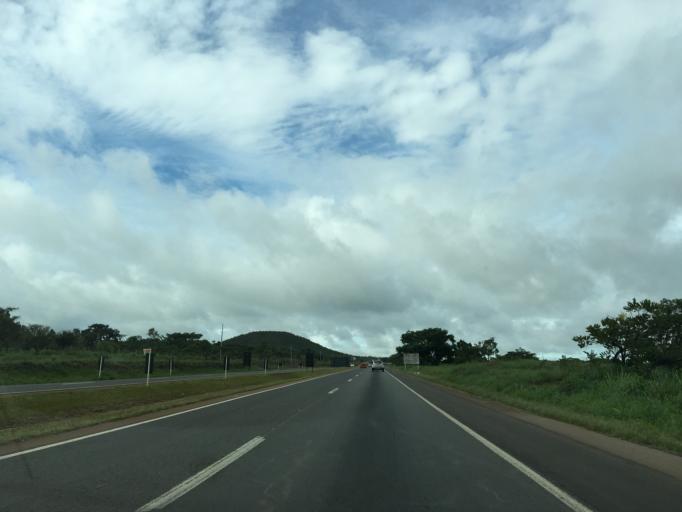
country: BR
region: Goias
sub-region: Abadiania
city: Abadiania
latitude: -16.1090
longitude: -48.3627
